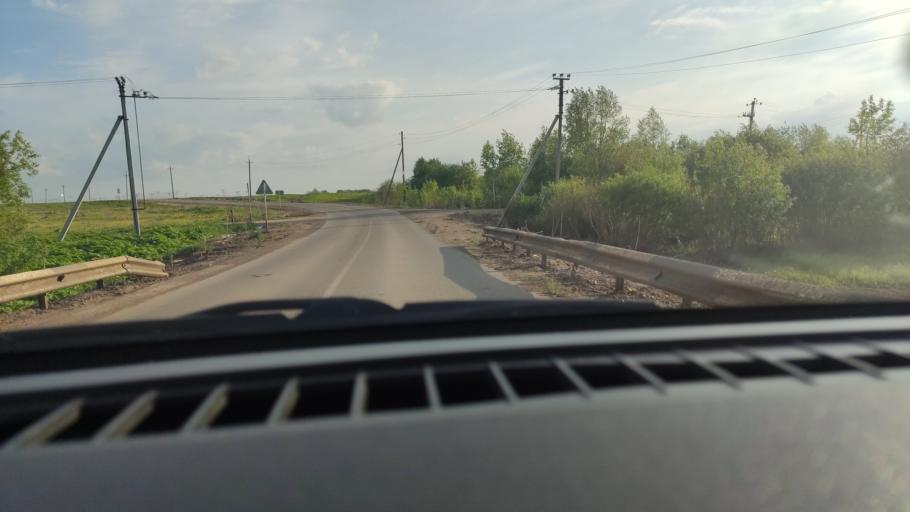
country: RU
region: Perm
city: Kultayevo
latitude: 57.8968
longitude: 55.9928
